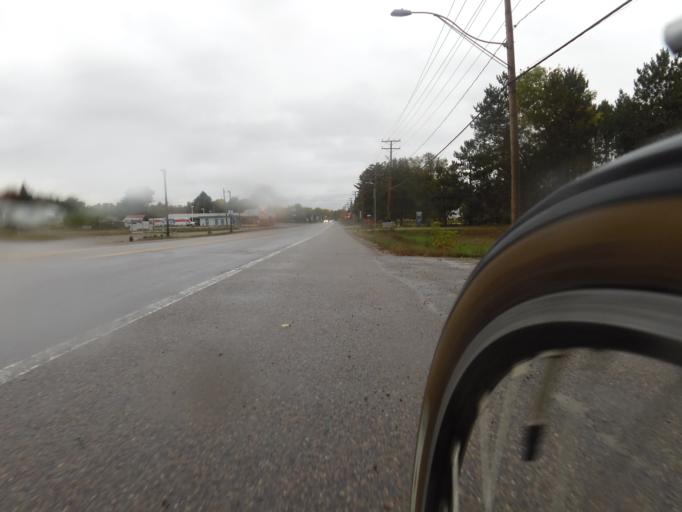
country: CA
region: Quebec
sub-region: Outaouais
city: Fort-Coulonge
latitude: 45.8518
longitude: -76.7315
